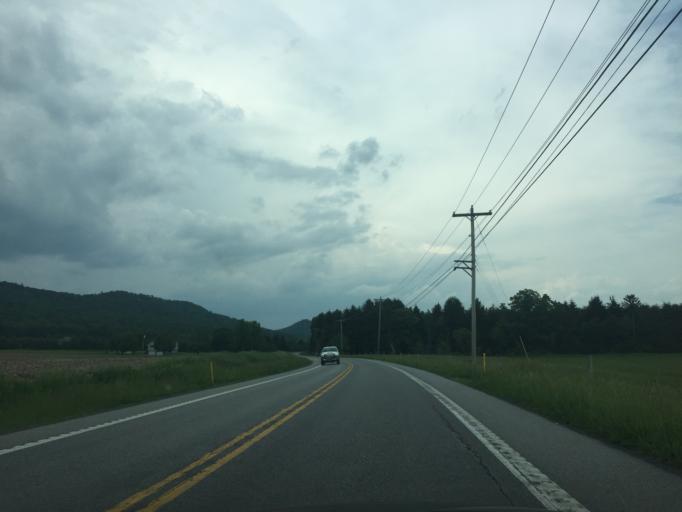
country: US
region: Pennsylvania
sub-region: Fulton County
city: McConnellsburg
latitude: 39.9864
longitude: -77.9672
